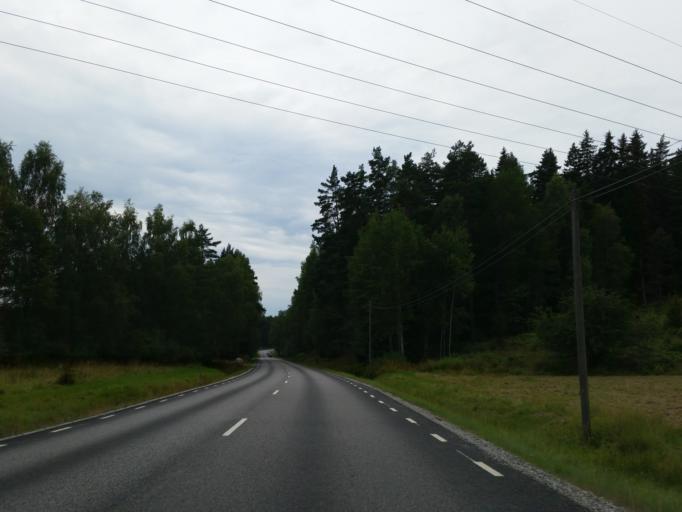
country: SE
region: Stockholm
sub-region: Salems Kommun
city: Ronninge
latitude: 59.2264
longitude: 17.6826
